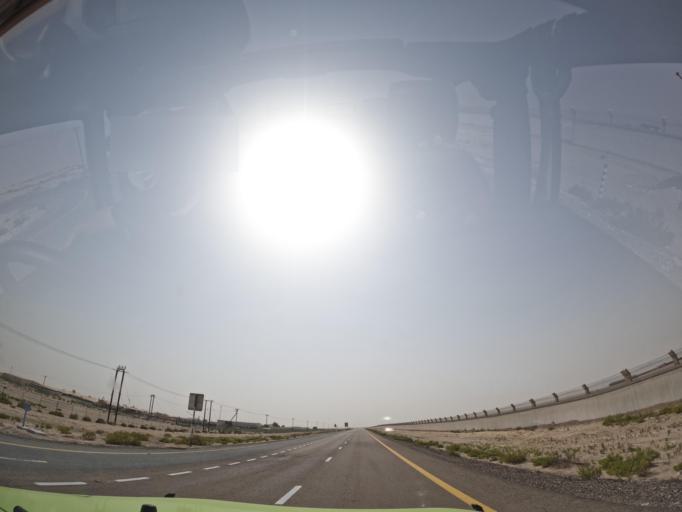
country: AE
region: Dubai
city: Dubai
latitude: 24.6666
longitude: 55.1759
